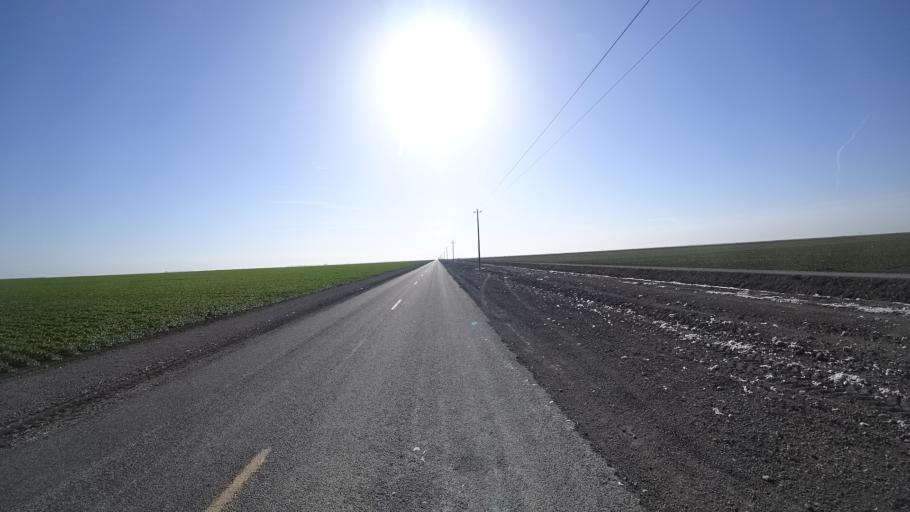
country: US
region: California
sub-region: Kings County
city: Stratford
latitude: 36.0797
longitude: -119.7421
